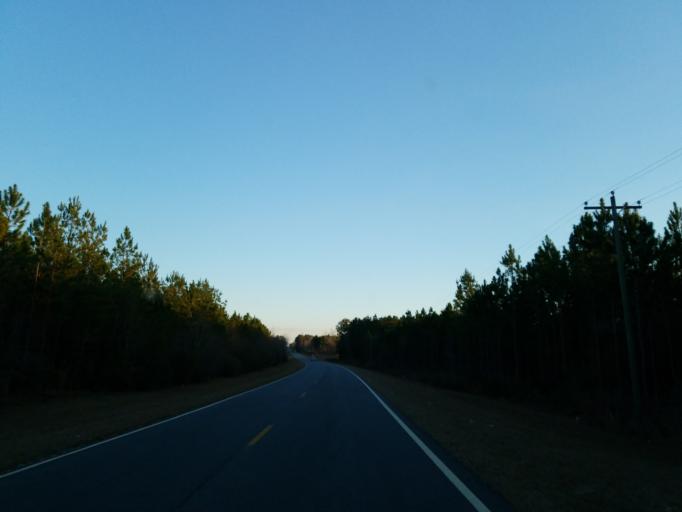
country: US
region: Georgia
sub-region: Tift County
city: Tifton
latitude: 31.5203
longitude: -83.5882
